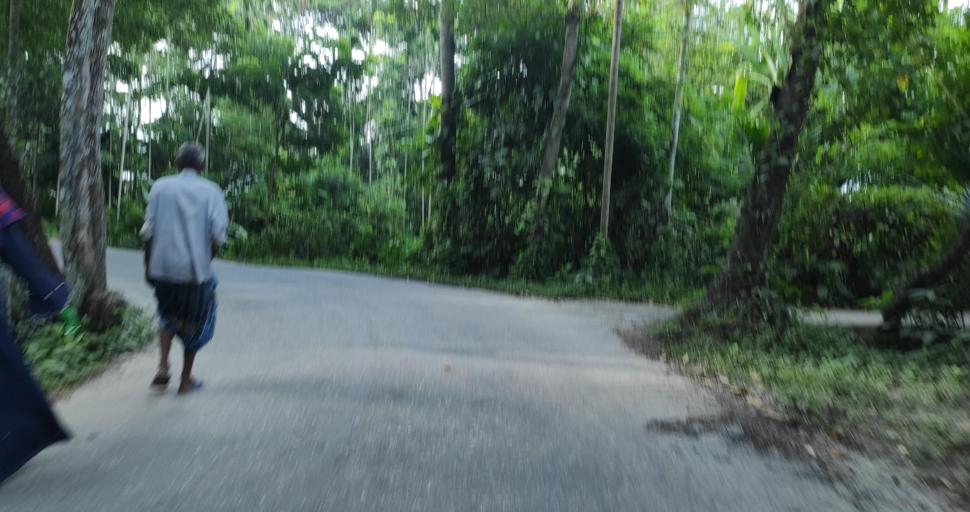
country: BD
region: Barisal
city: Gaurnadi
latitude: 22.8979
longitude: 90.1823
